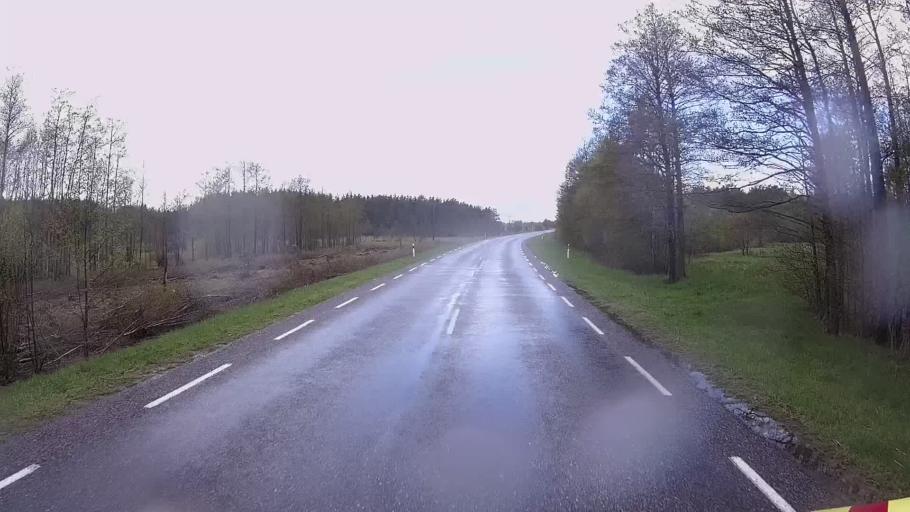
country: EE
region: Hiiumaa
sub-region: Kaerdla linn
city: Kardla
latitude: 58.8325
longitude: 22.8197
